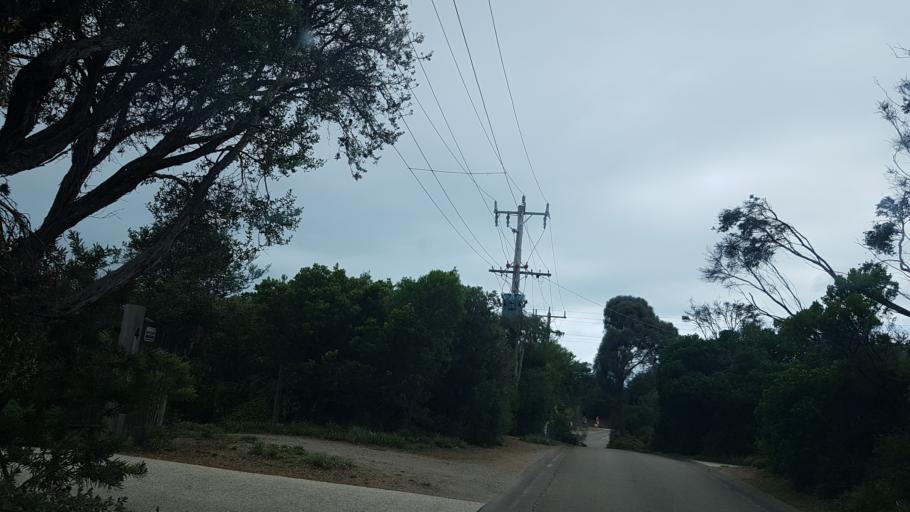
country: AU
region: Victoria
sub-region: Mornington Peninsula
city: Blairgowrie
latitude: -38.3768
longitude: 144.7794
